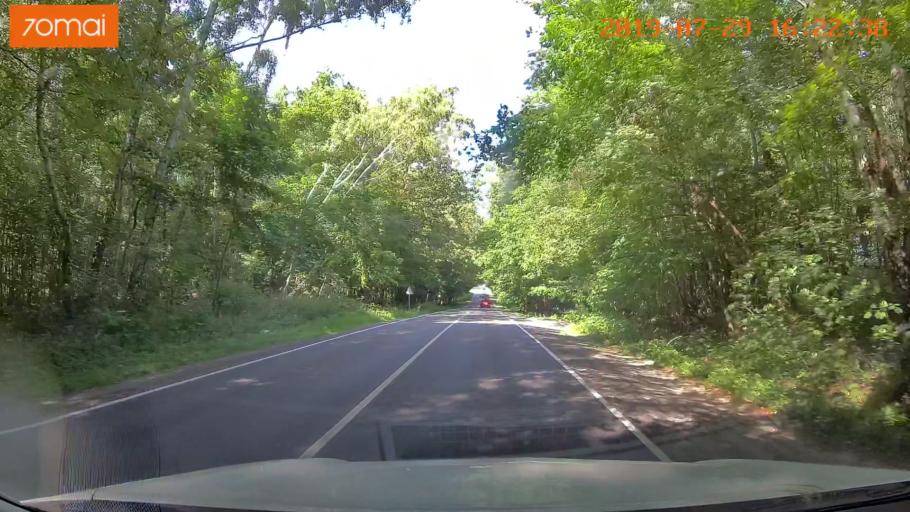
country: RU
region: Kaliningrad
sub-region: Gorod Kaliningrad
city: Baltiysk
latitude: 54.6996
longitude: 19.9400
